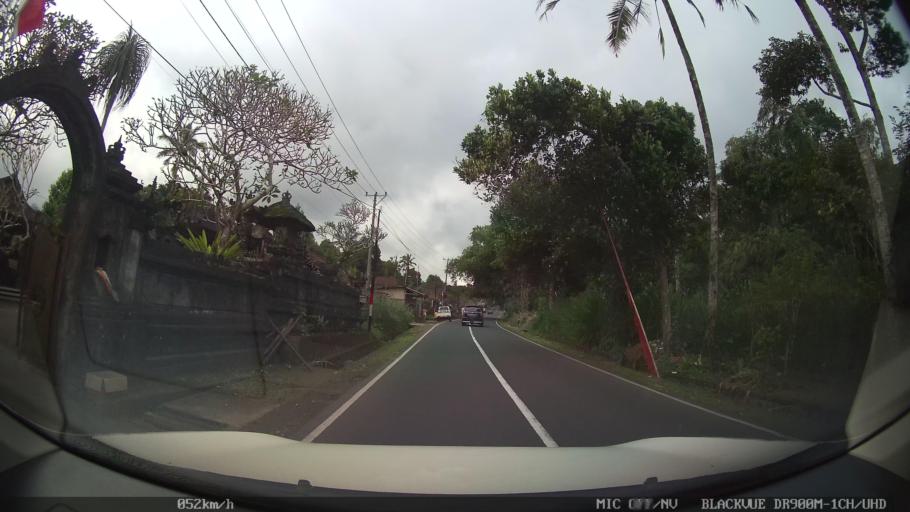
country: ID
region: Bali
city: Banjar Tiga
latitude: -8.3805
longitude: 115.4177
